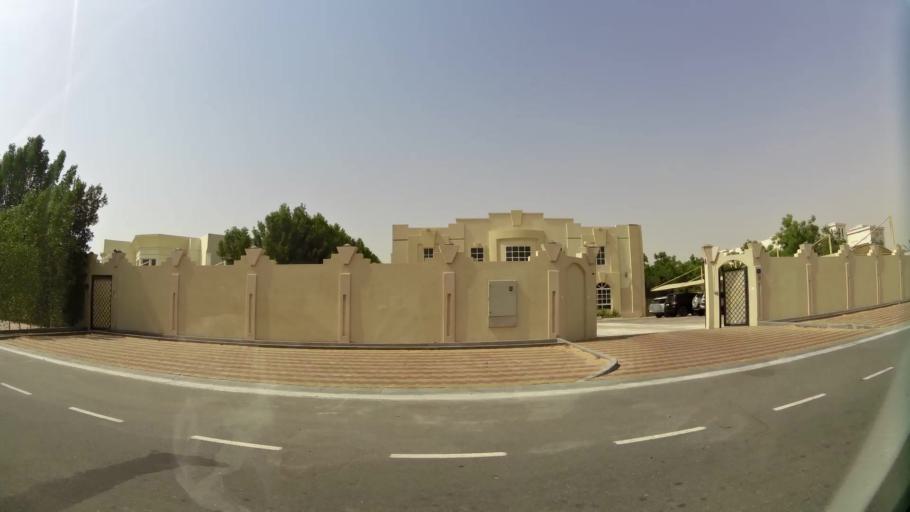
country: AE
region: Ash Shariqah
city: Sharjah
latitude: 25.2414
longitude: 55.4815
